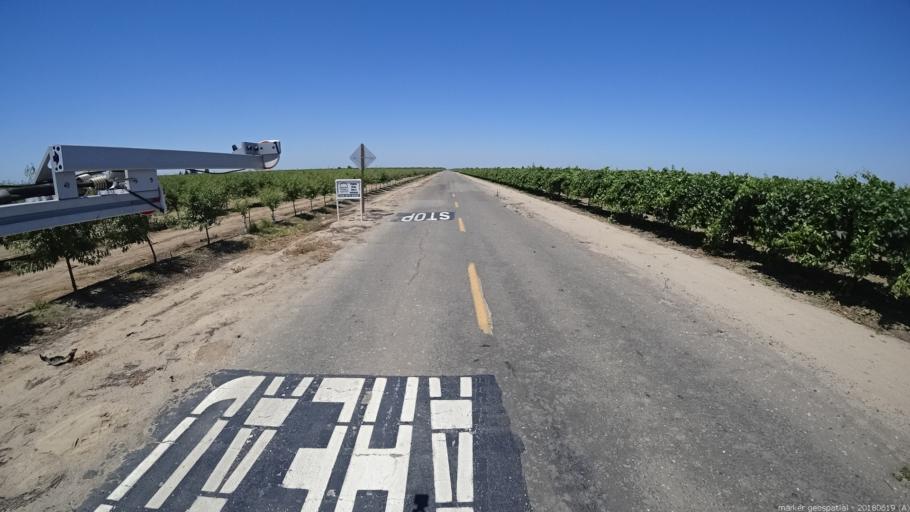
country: US
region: California
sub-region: Madera County
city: Parkwood
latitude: 36.8731
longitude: -120.0579
